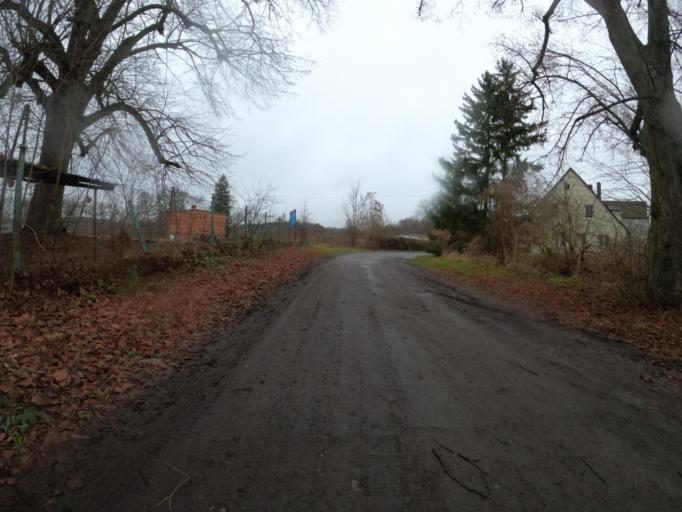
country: PL
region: West Pomeranian Voivodeship
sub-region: Powiat mysliborski
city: Debno
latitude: 52.7837
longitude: 14.7667
